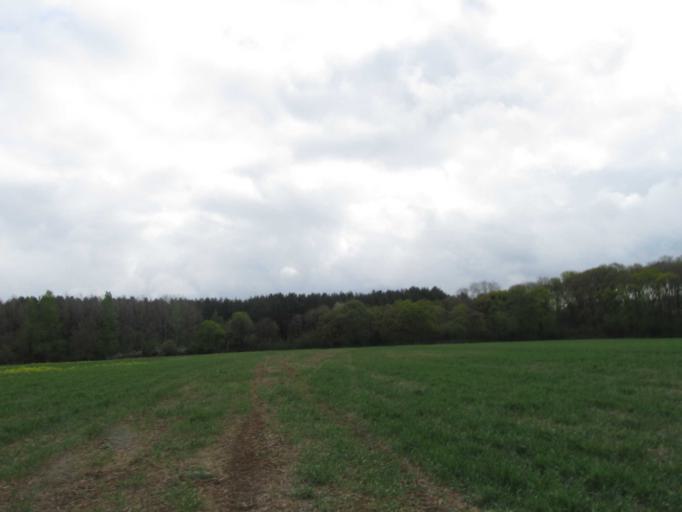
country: GB
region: England
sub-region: Surrey
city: Chiddingfold
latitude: 51.0722
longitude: -0.6342
